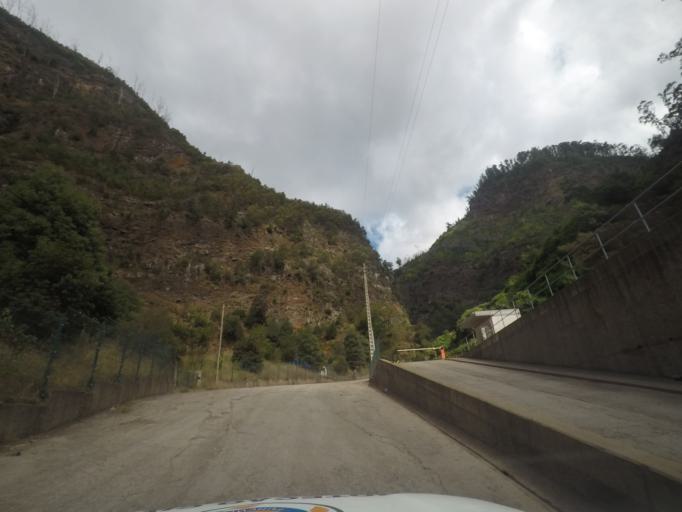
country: PT
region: Madeira
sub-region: Funchal
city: Nossa Senhora do Monte
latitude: 32.6847
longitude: -16.9153
